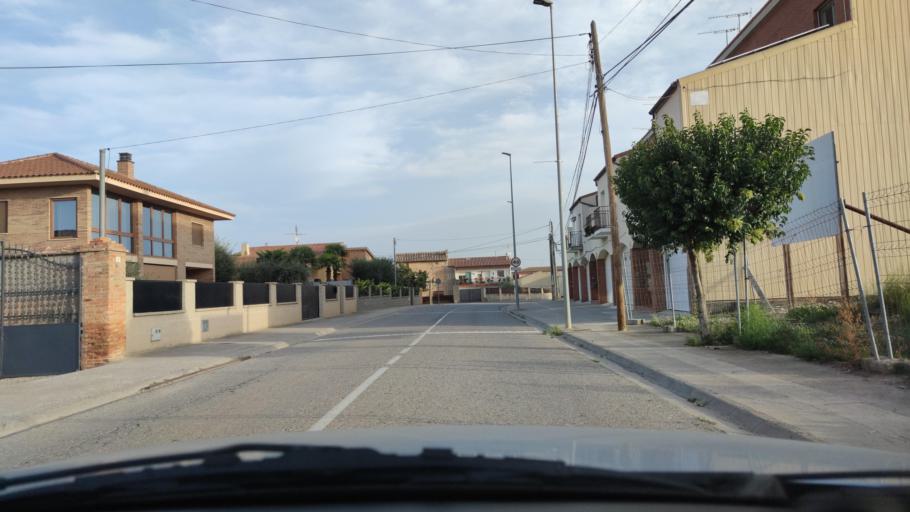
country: ES
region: Catalonia
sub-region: Provincia de Lleida
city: Anglesola
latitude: 41.6545
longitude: 1.0814
